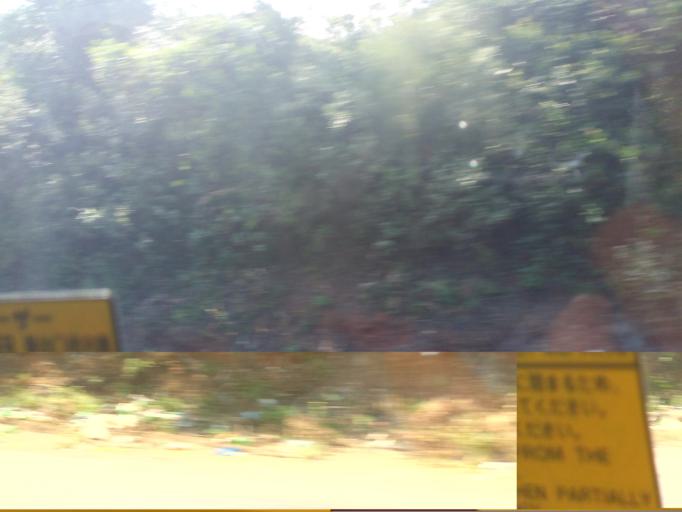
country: KE
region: Nakuru
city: Kijabe
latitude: -1.0118
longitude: 36.6011
